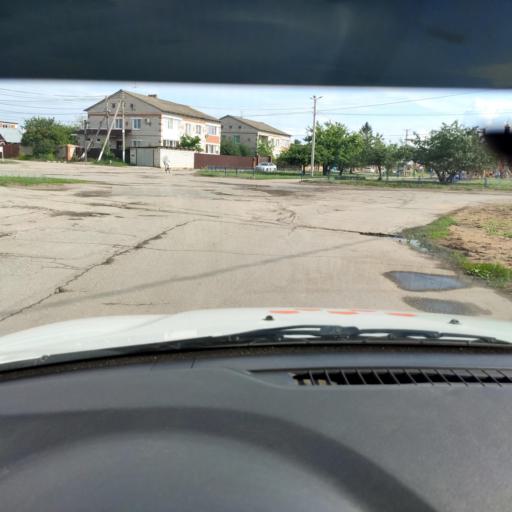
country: RU
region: Samara
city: Podstepki
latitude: 53.6121
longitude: 49.0395
